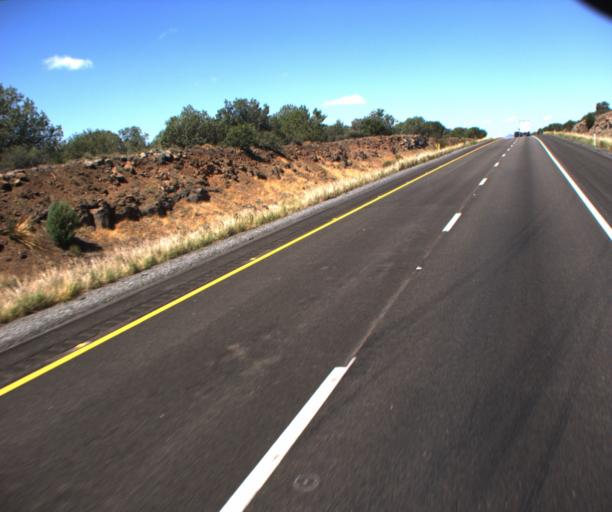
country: US
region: Arizona
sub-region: Mohave County
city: Peach Springs
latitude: 35.1902
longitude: -113.3243
